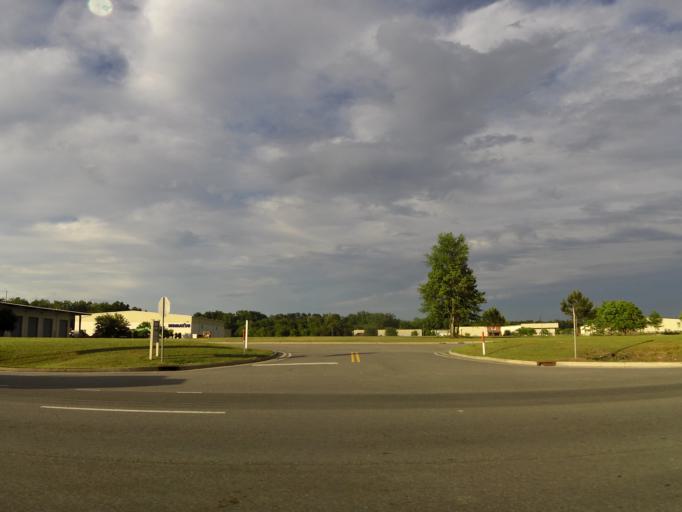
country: US
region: Georgia
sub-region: Chatham County
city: Pooler
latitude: 32.1046
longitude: -81.2265
